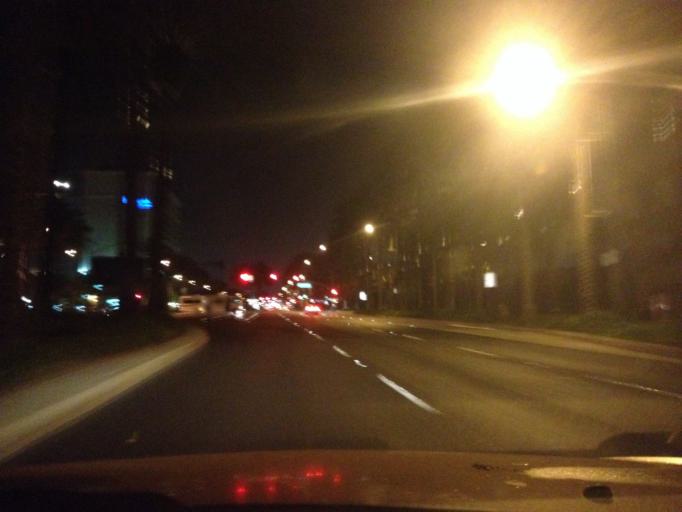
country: US
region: California
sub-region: Orange County
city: Anaheim
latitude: 33.8033
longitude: -117.9116
